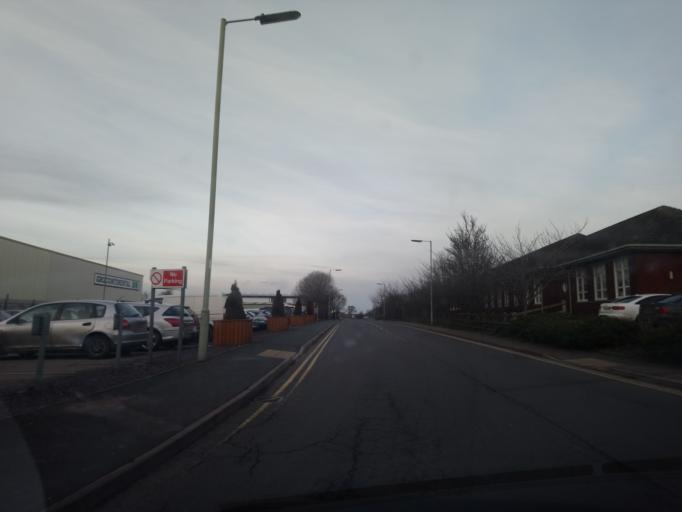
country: GB
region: England
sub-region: Shropshire
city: Whitchurch
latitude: 52.9642
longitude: -2.6644
